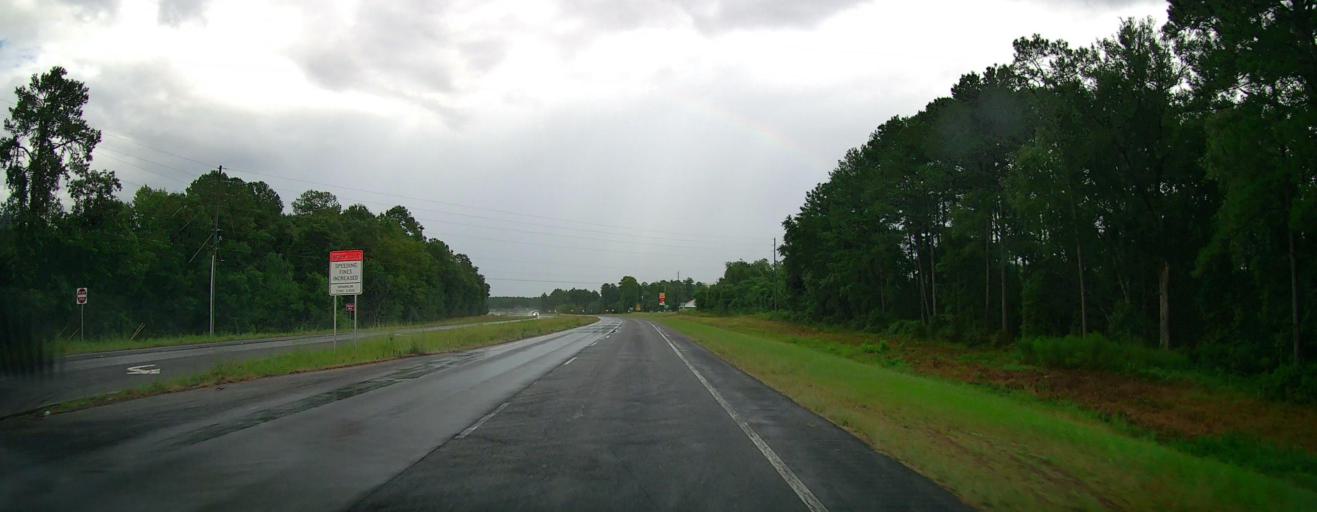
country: US
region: Georgia
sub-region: Ware County
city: Deenwood
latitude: 31.2547
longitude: -82.4827
